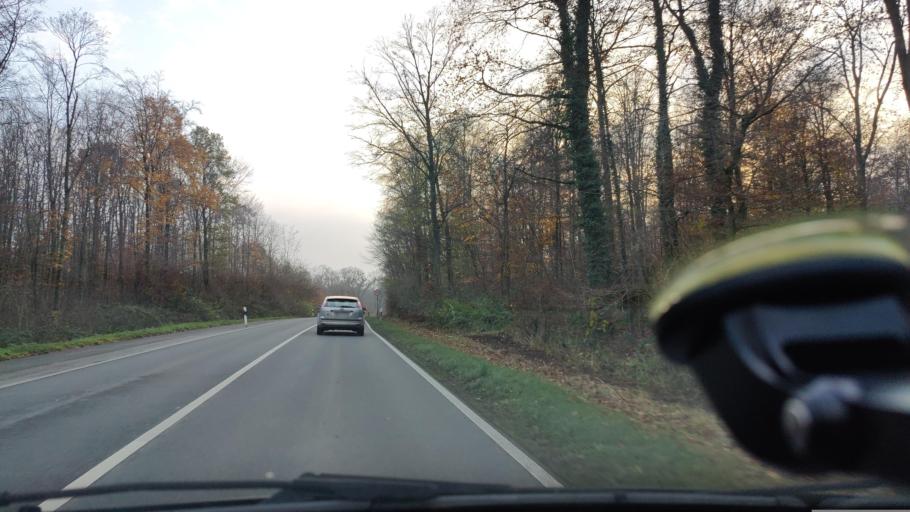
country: DE
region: North Rhine-Westphalia
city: Lunen
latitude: 51.6459
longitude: 7.5334
